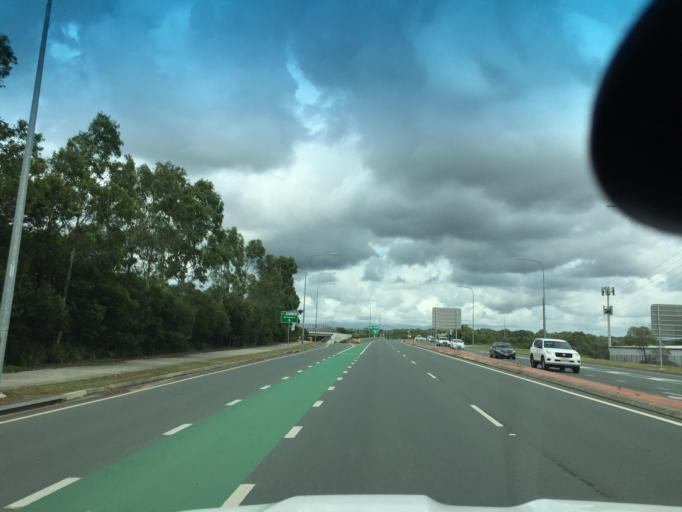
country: AU
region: Queensland
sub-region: Moreton Bay
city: Deception Bay
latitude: -27.2096
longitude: 152.9958
